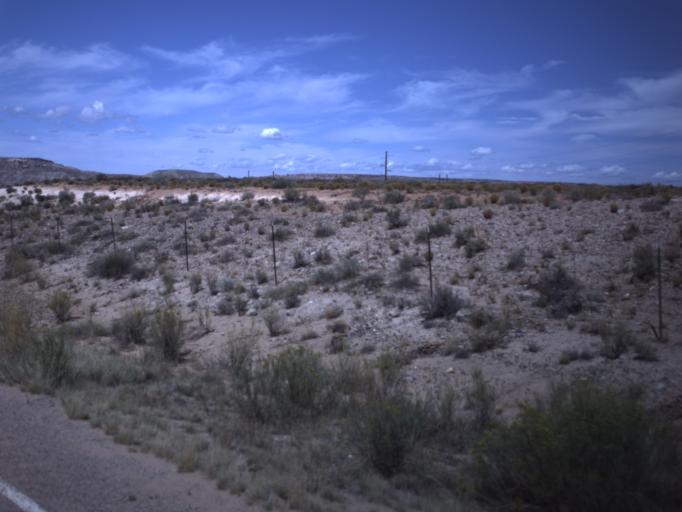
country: US
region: Utah
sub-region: San Juan County
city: Blanding
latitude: 37.2804
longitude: -109.3753
